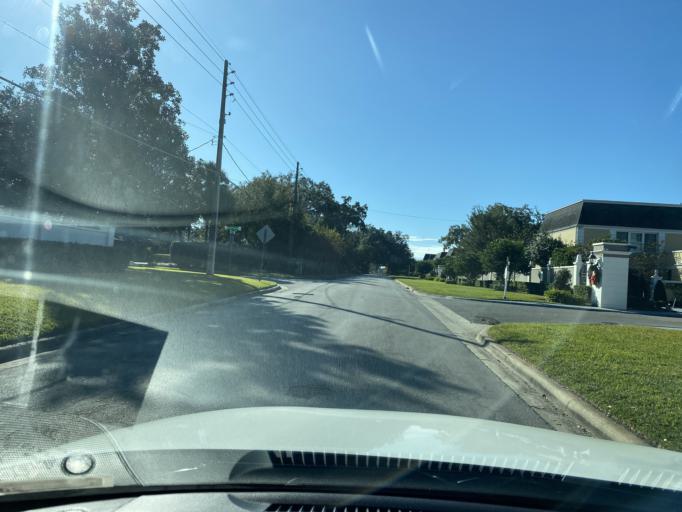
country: US
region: Florida
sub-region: Orange County
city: Orlando
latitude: 28.5564
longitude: -81.4057
